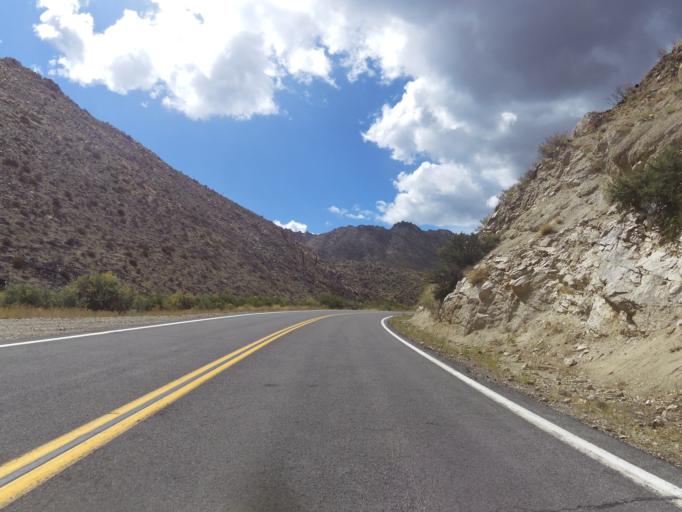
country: US
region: Nevada
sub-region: Lyon County
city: Smith Valley
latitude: 38.6426
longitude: -119.5444
